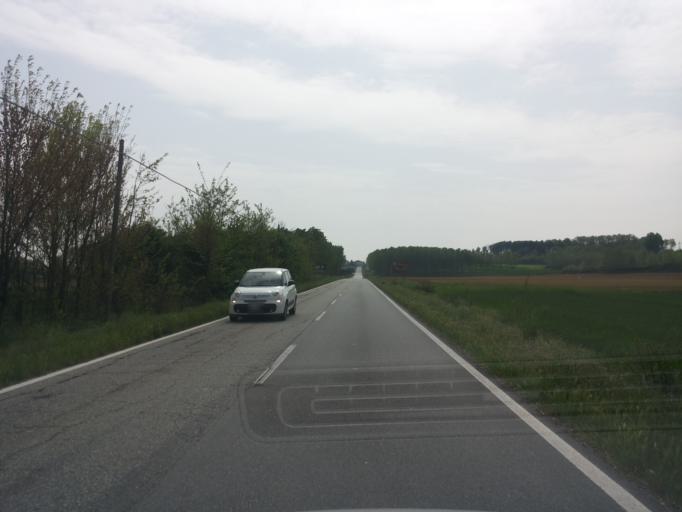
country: IT
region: Piedmont
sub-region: Provincia di Alessandria
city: Mirabello Monferrato
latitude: 45.0468
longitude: 8.5191
